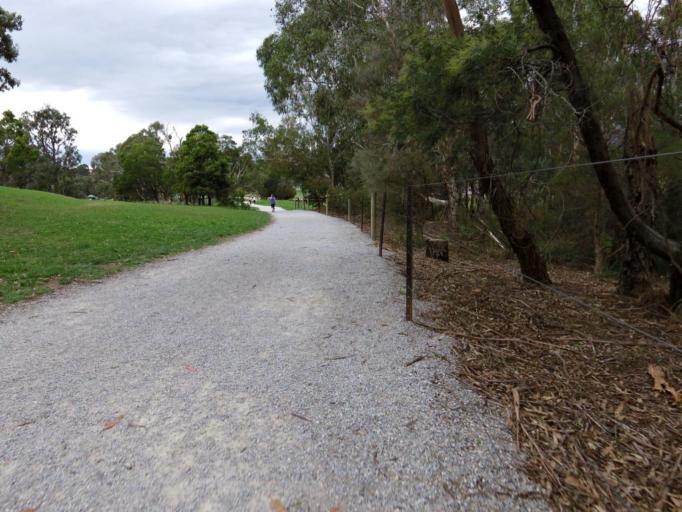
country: AU
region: Victoria
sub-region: Yarra Ranges
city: Lilydale
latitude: -37.7631
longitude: 145.3539
